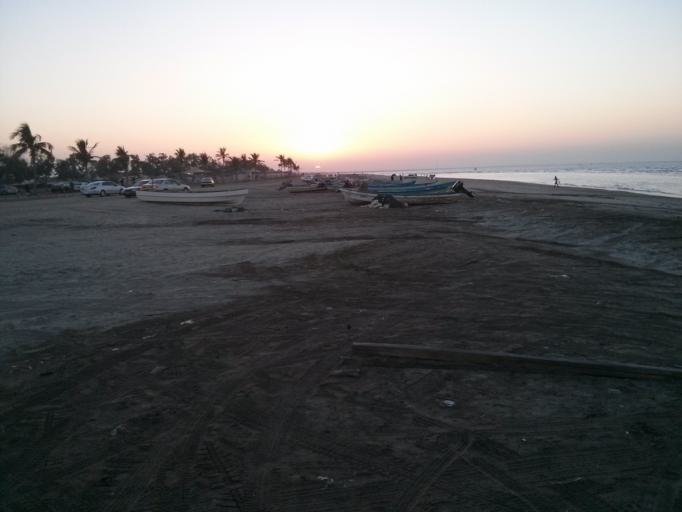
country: OM
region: Al Batinah
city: Barka'
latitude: 23.7823
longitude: 57.7906
